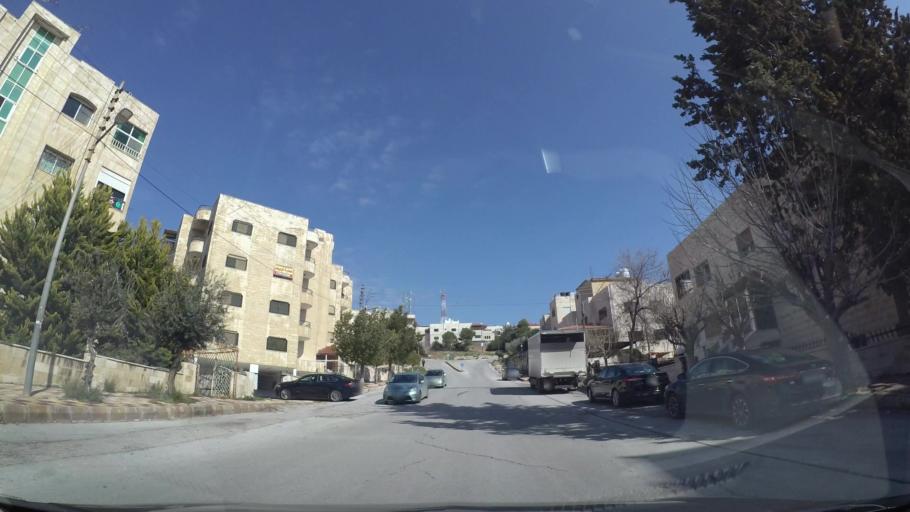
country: JO
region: Amman
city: Al Jubayhah
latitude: 31.9960
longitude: 35.8963
